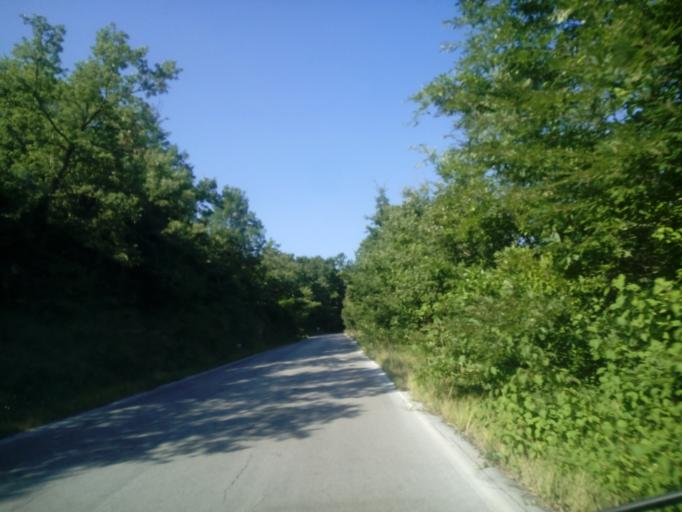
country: IT
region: Molise
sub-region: Provincia di Campobasso
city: Jelsi
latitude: 41.5111
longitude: 14.7785
